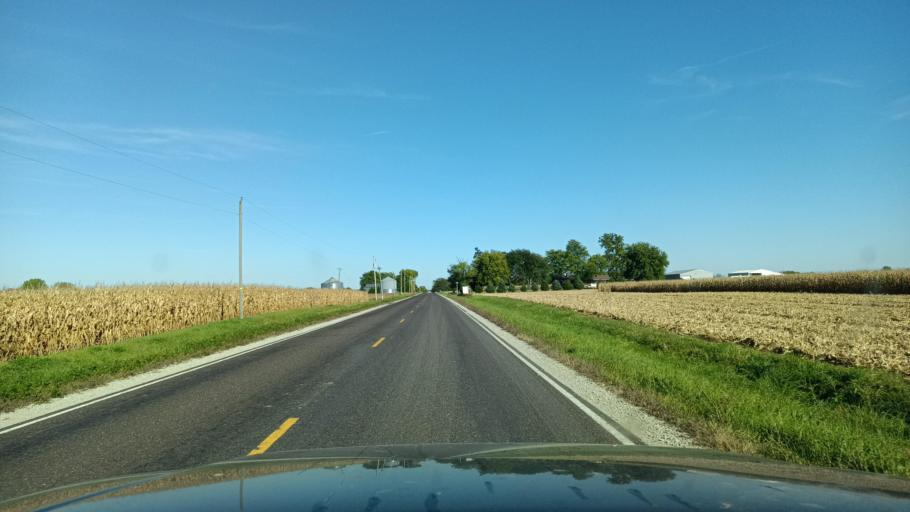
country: US
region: Illinois
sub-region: McLean County
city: Heyworth
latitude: 40.2315
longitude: -89.0163
